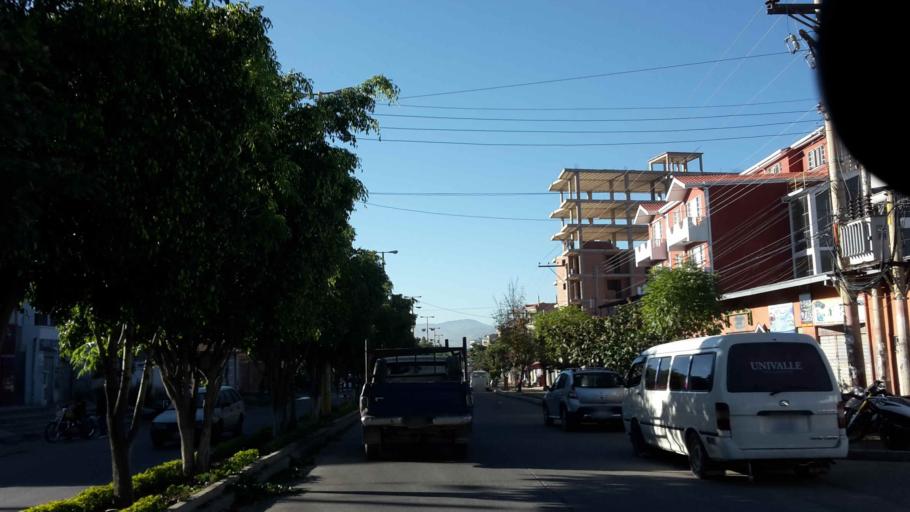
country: BO
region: Cochabamba
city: Cochabamba
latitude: -17.3521
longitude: -66.1919
